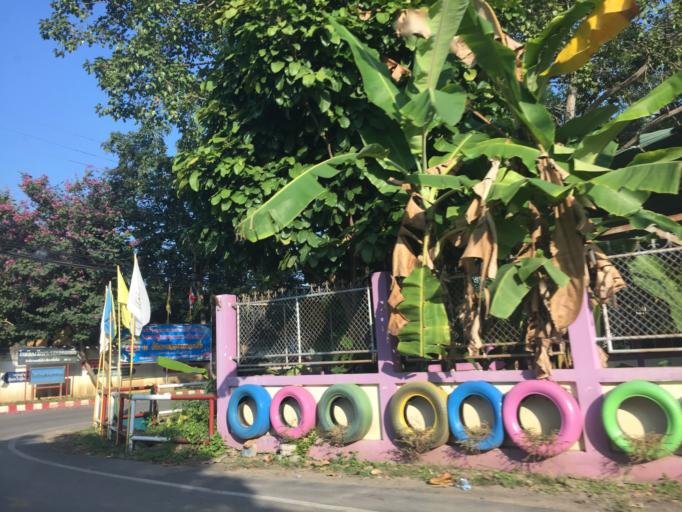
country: TH
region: Chiang Mai
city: Saraphi
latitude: 18.7389
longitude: 99.0134
